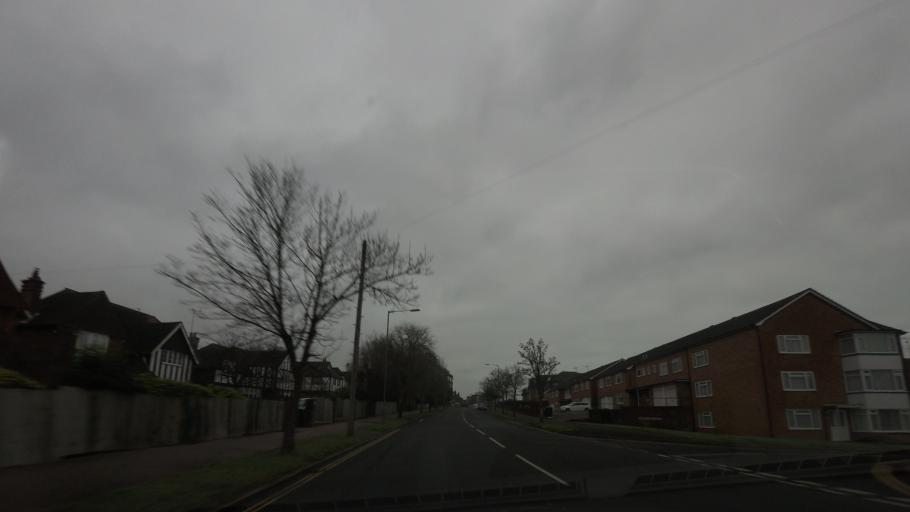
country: GB
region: England
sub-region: East Sussex
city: Bexhill-on-Sea
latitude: 50.8413
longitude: 0.4525
